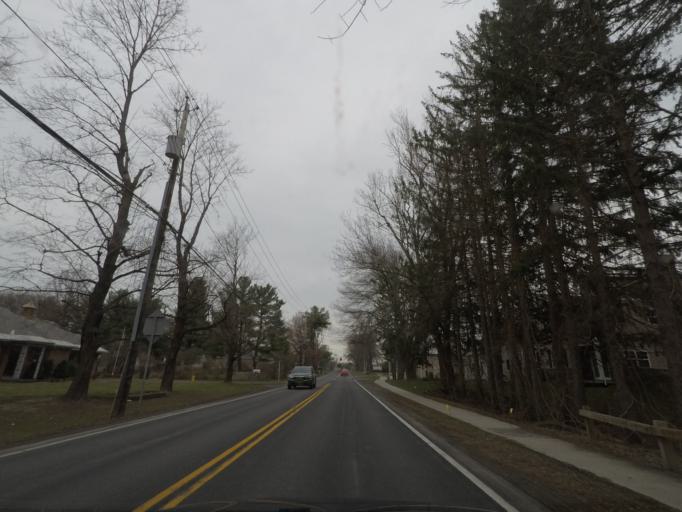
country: US
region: New York
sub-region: Albany County
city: Delmar
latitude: 42.6017
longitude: -73.7969
